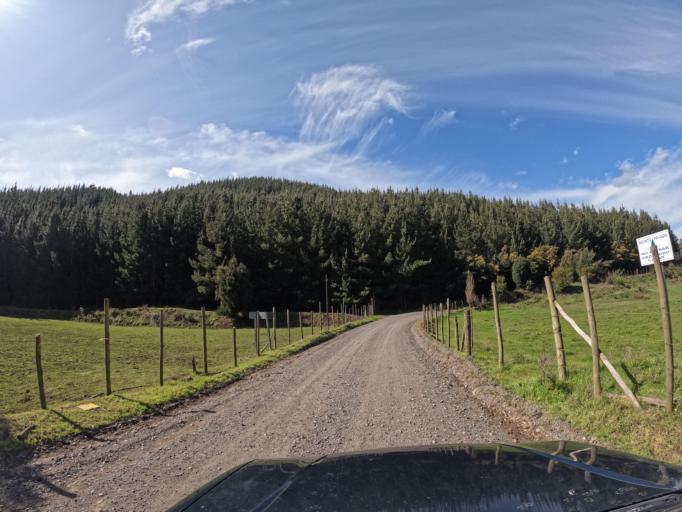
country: CL
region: Biobio
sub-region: Provincia de Concepcion
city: Chiguayante
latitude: -37.0626
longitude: -72.8986
